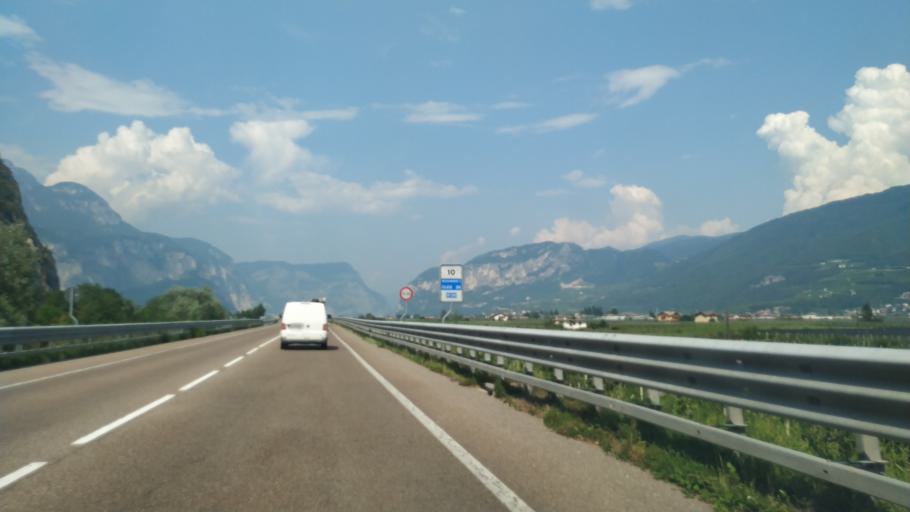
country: IT
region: Trentino-Alto Adige
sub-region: Provincia di Trento
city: Nave San Rocco
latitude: 46.1695
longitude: 11.0866
